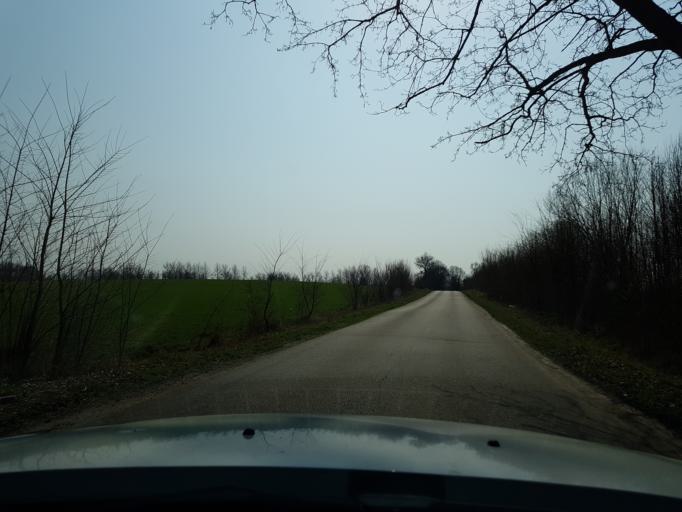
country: PL
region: West Pomeranian Voivodeship
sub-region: Powiat koszalinski
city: Sianow
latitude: 54.2560
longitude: 16.3123
